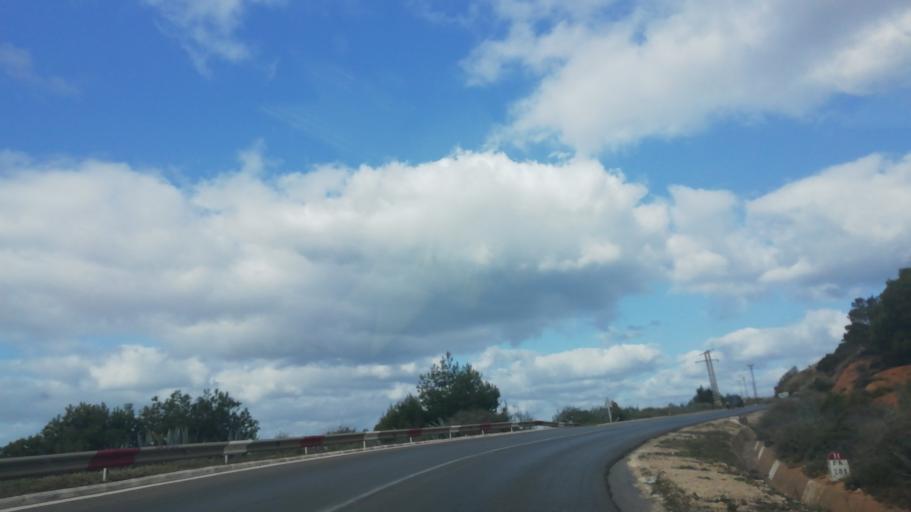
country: DZ
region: Relizane
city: Mazouna
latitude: 36.3075
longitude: 0.6700
